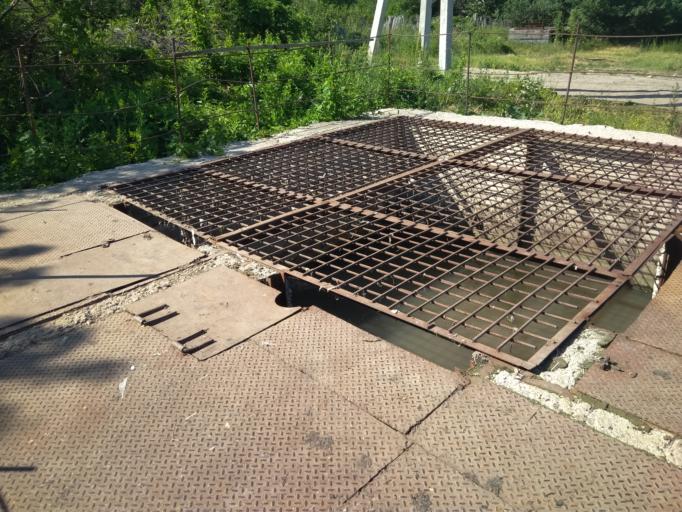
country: RU
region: Ulyanovsk
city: Novoul'yanovsk
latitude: 54.2368
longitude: 48.3456
